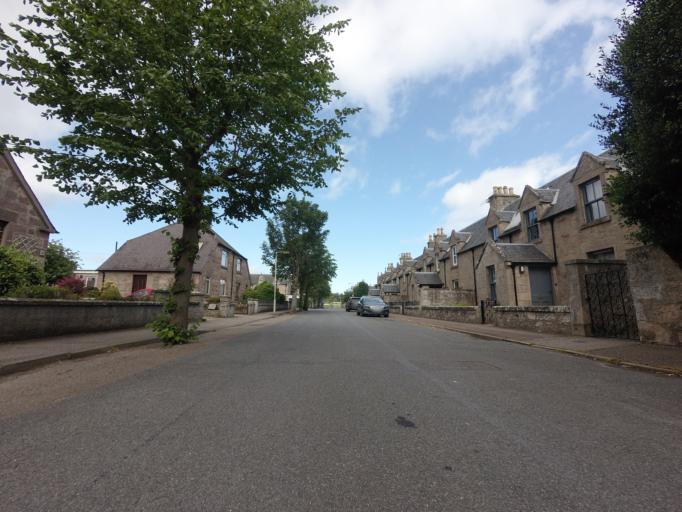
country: GB
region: Scotland
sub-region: Highland
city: Nairn
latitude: 57.5806
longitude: -3.8721
